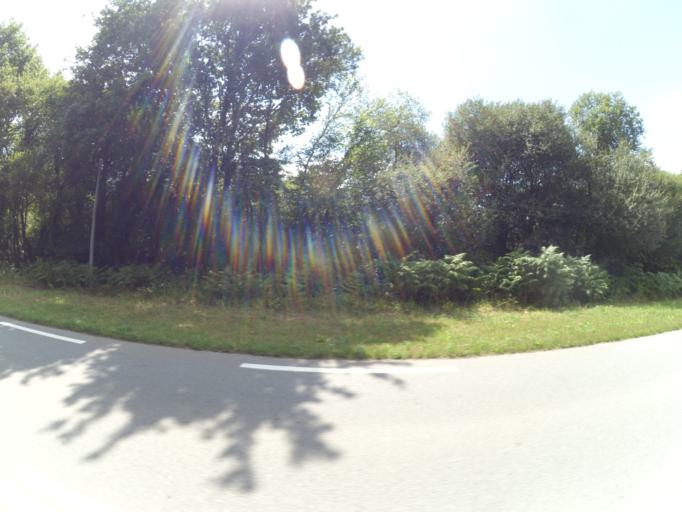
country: FR
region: Brittany
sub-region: Departement du Morbihan
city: Landevant
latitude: 47.7549
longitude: -3.1103
